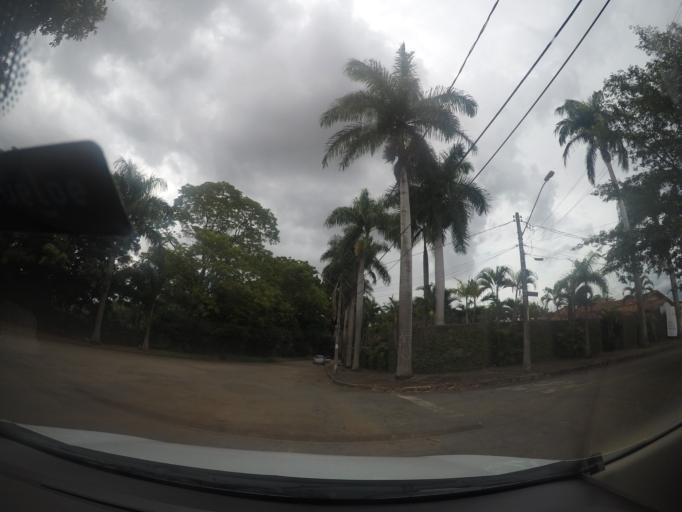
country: BR
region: Goias
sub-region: Goiania
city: Goiania
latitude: -16.6528
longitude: -49.2338
